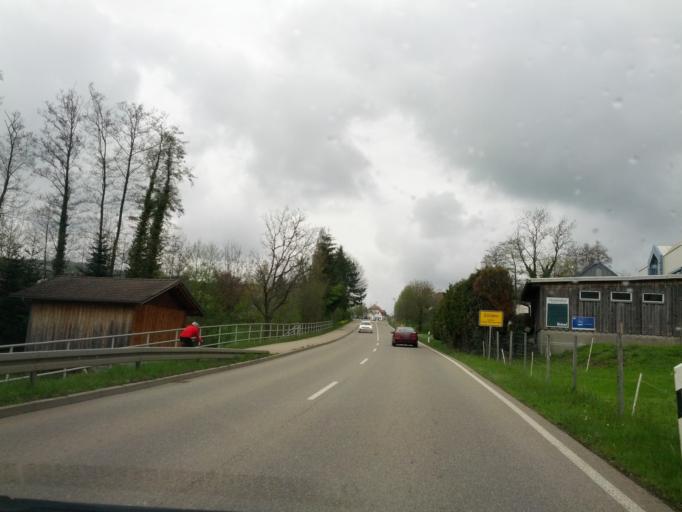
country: DE
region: Baden-Wuerttemberg
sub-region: Freiburg Region
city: Solden
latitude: 47.9294
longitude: 7.8081
